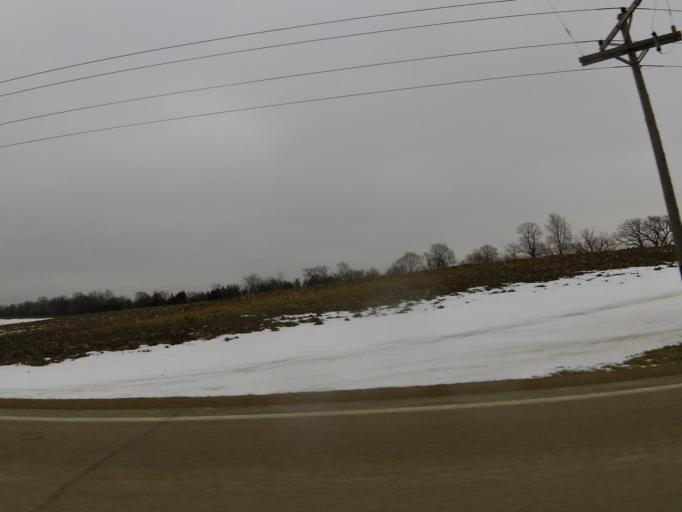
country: US
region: Minnesota
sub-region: Carver County
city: Carver
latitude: 44.7431
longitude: -93.6841
